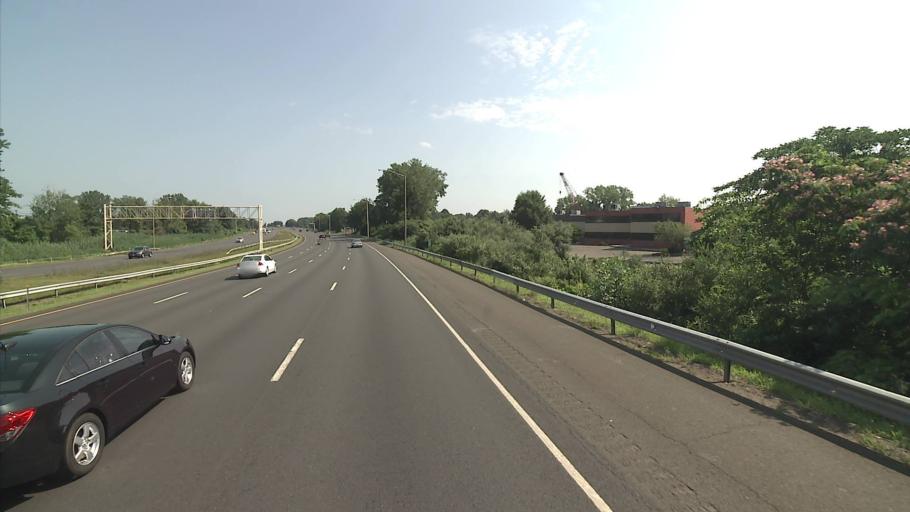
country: US
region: Connecticut
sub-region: New Haven County
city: North Haven
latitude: 41.3428
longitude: -72.8694
